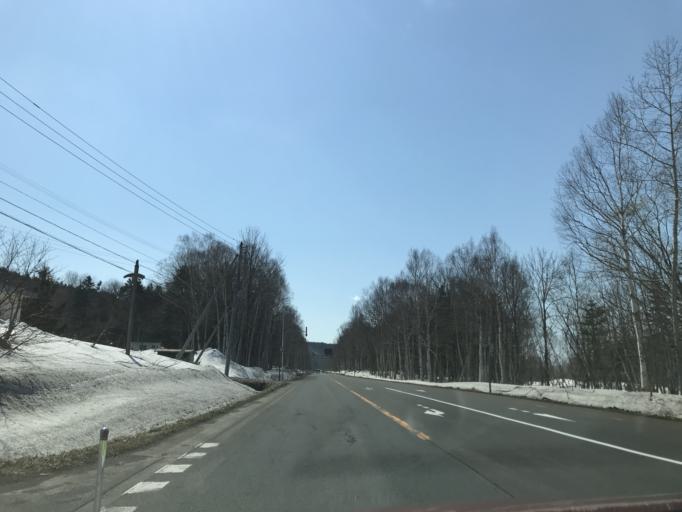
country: JP
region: Hokkaido
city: Nayoro
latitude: 44.7189
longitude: 142.2711
